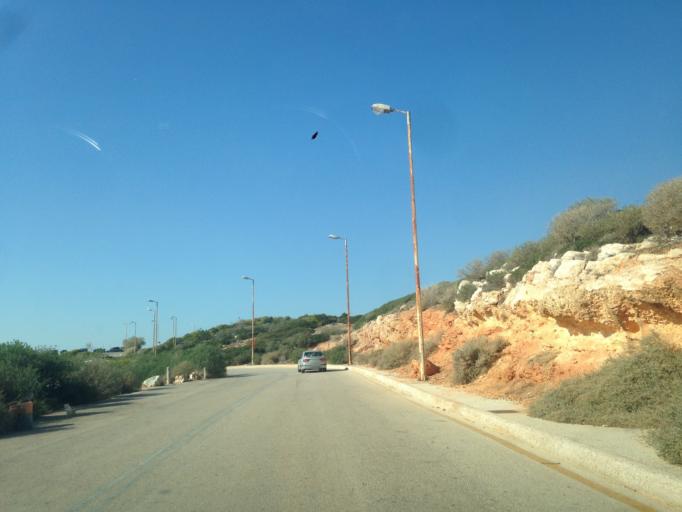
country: GR
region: Attica
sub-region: Nomarchia Anatolikis Attikis
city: Vouliagmeni
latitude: 37.7981
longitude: 23.7741
